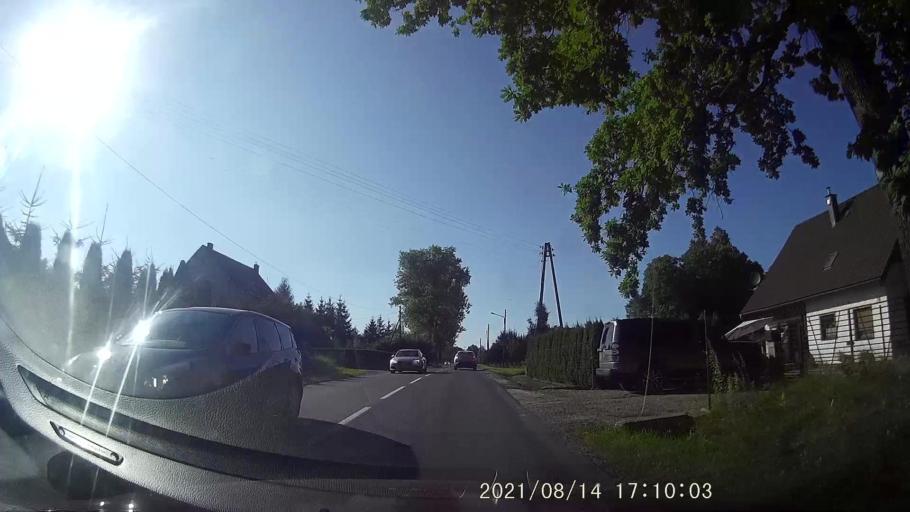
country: PL
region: Lower Silesian Voivodeship
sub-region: Powiat jeleniogorski
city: Myslakowice
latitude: 50.8258
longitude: 15.8007
